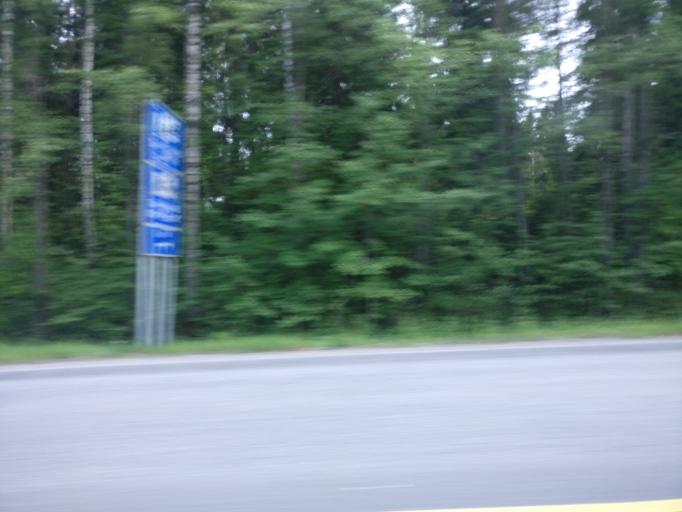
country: FI
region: Southern Savonia
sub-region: Savonlinna
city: Savonlinna
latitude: 61.8674
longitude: 28.9325
